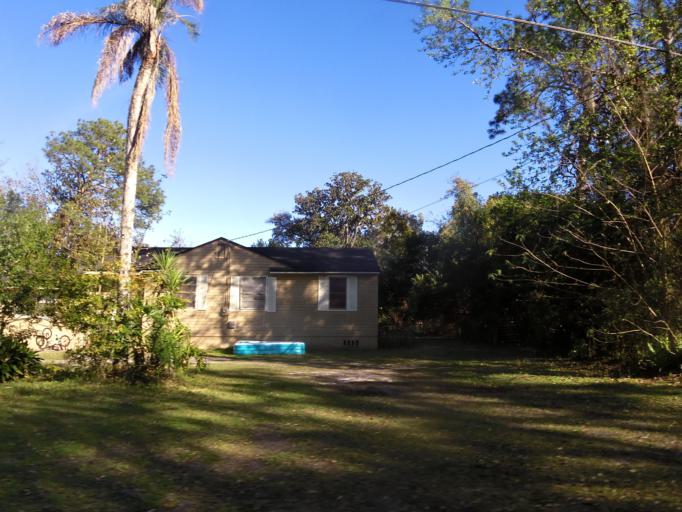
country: US
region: Florida
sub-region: Duval County
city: Jacksonville
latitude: 30.4013
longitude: -81.6744
